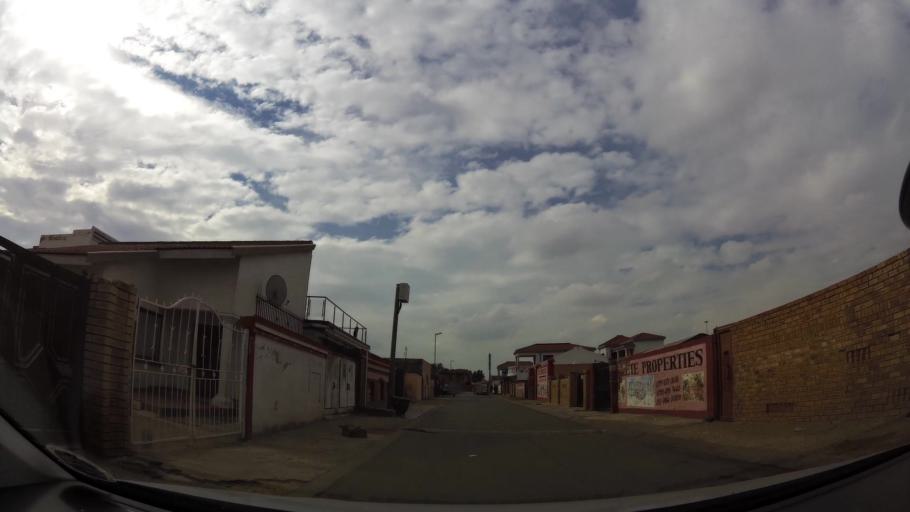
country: ZA
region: Gauteng
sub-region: City of Johannesburg Metropolitan Municipality
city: Soweto
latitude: -26.2672
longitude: 27.8543
